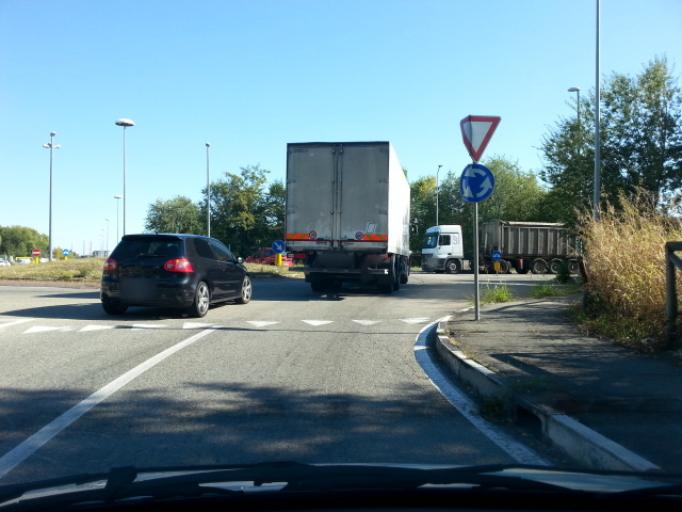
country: IT
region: Piedmont
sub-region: Provincia di Torino
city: Fornaci
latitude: 45.0428
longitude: 7.5910
